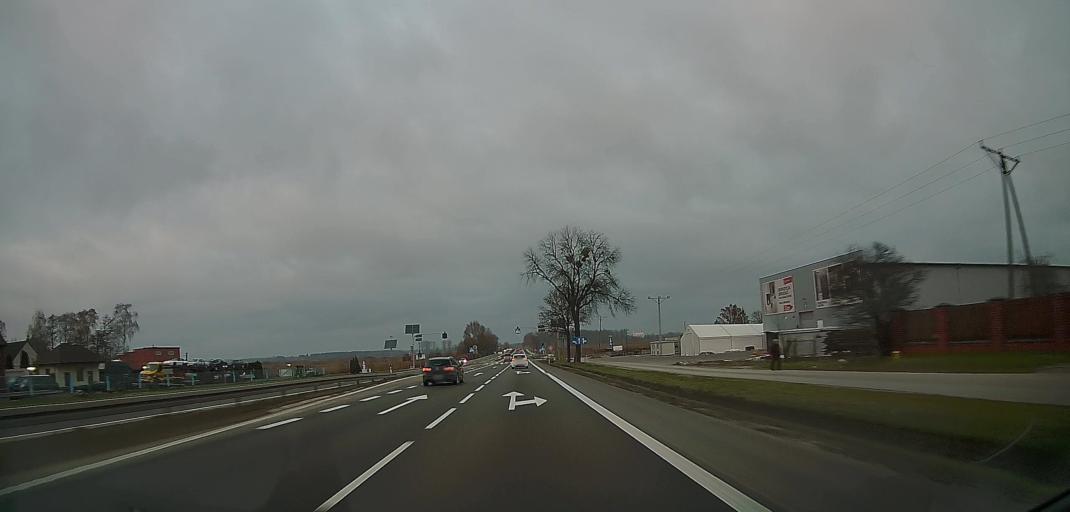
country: PL
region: Masovian Voivodeship
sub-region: Powiat radomski
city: Jedlinsk
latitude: 51.4935
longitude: 21.1196
